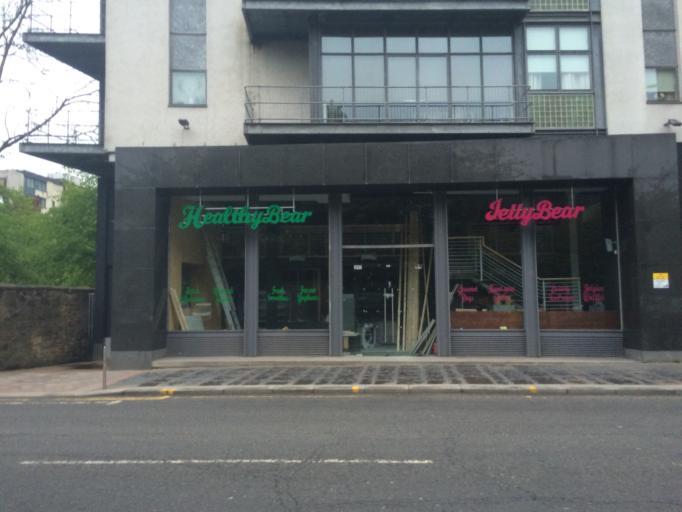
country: GB
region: Scotland
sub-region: Glasgow City
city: Glasgow
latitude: 55.8595
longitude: -4.2444
